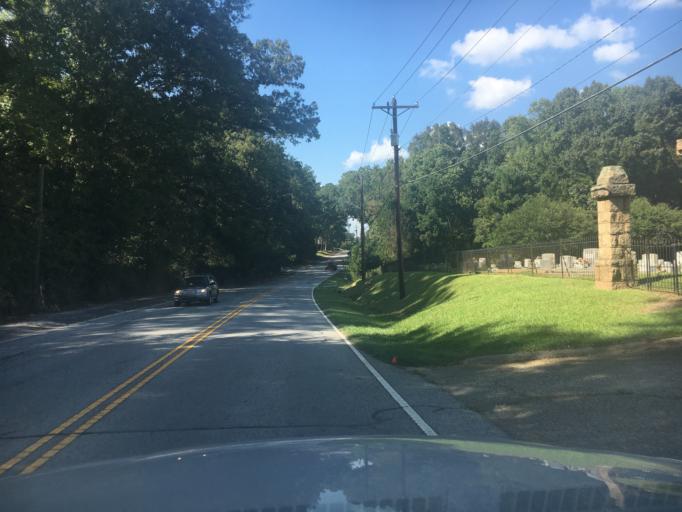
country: US
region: South Carolina
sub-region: Greenwood County
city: Greenwood
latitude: 34.2069
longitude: -82.1643
